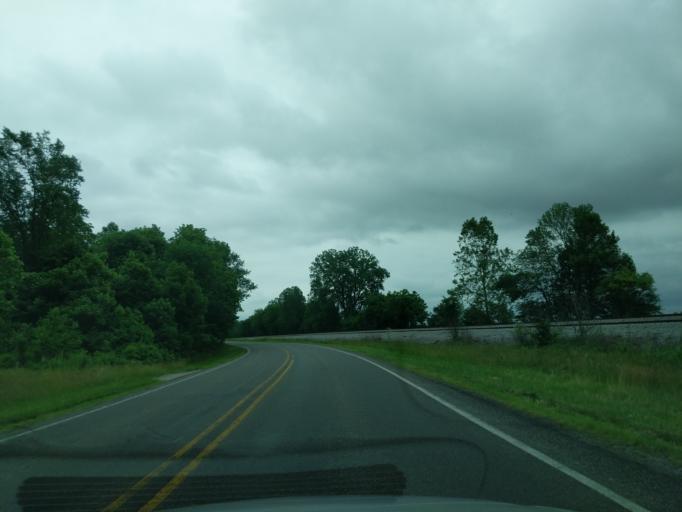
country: US
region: Indiana
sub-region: Madison County
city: Elwood
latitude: 40.2827
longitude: -85.9401
